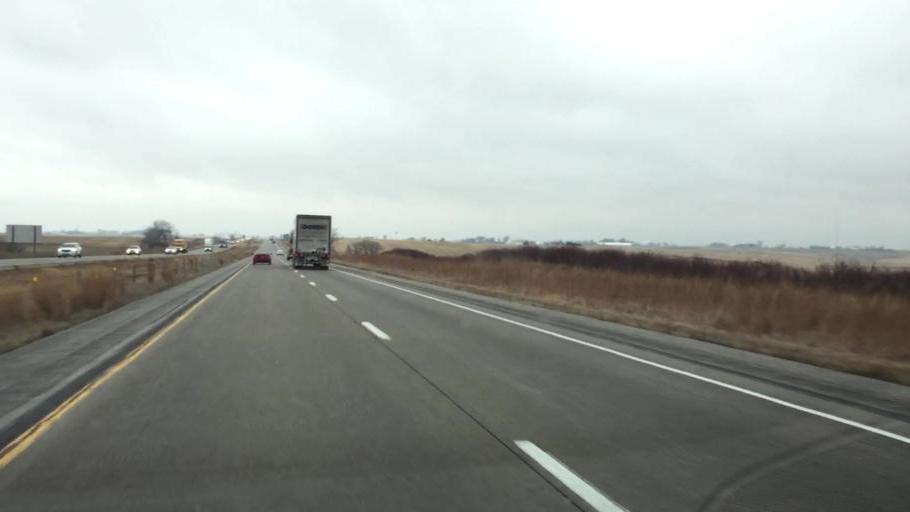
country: US
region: Iowa
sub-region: Iowa County
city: Williamsburg
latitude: 41.6871
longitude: -91.9739
